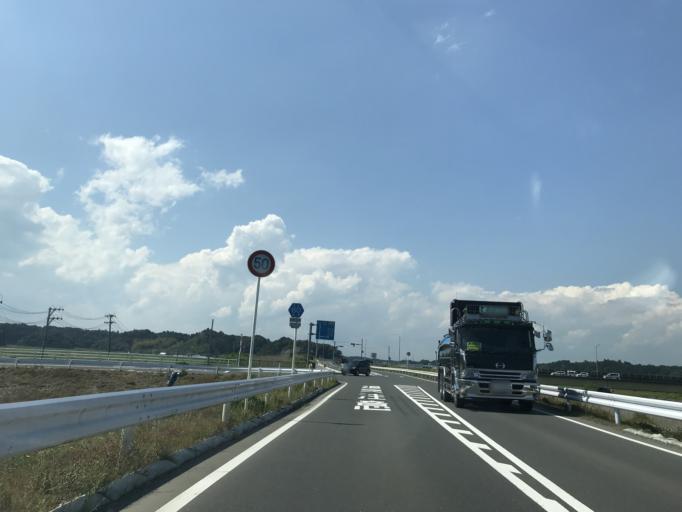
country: JP
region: Miyagi
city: Yamoto
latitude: 38.3941
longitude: 141.1563
